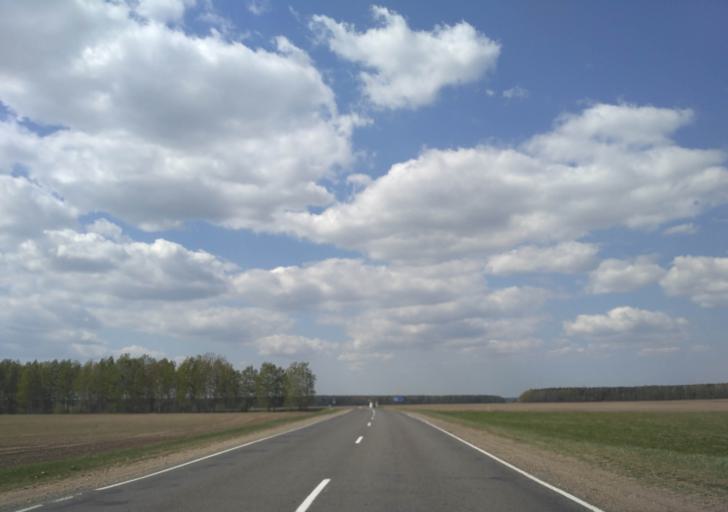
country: BY
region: Minsk
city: Vilyeyka
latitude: 54.5168
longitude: 27.0347
